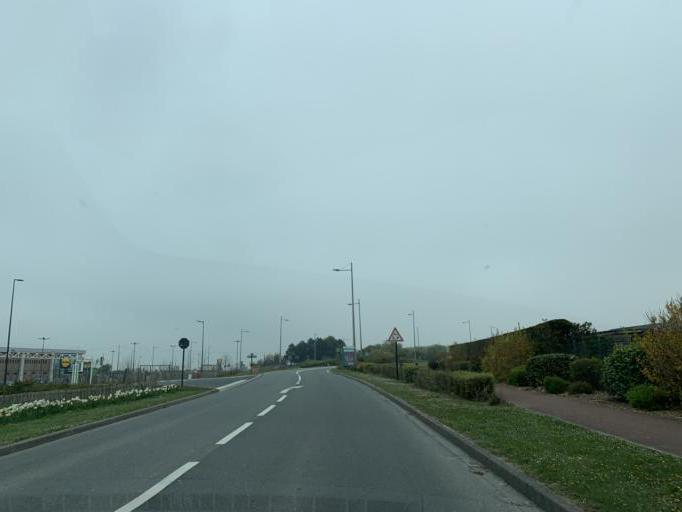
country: FR
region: Nord-Pas-de-Calais
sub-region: Departement du Pas-de-Calais
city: Marquise
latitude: 50.8228
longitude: 1.7065
